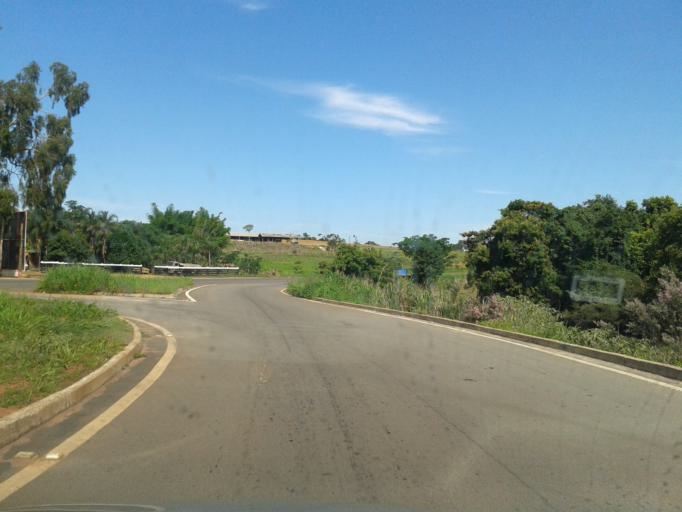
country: BR
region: Goias
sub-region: Piracanjuba
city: Piracanjuba
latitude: -17.2308
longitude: -48.7116
